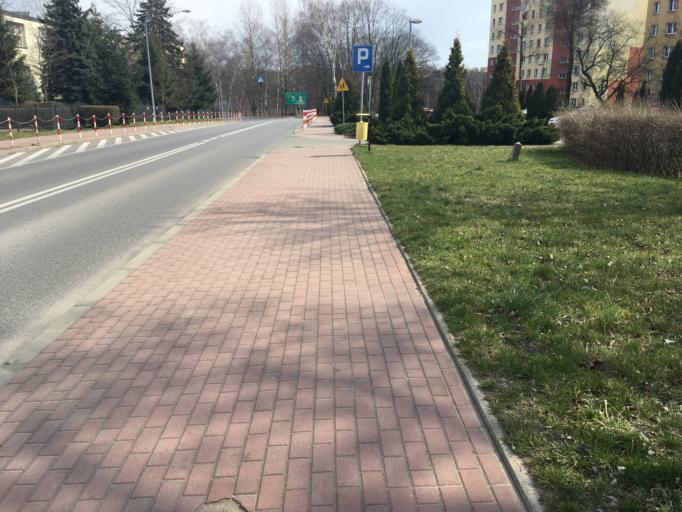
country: PL
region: Swietokrzyskie
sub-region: Powiat starachowicki
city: Starachowice
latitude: 51.0544
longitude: 21.0620
